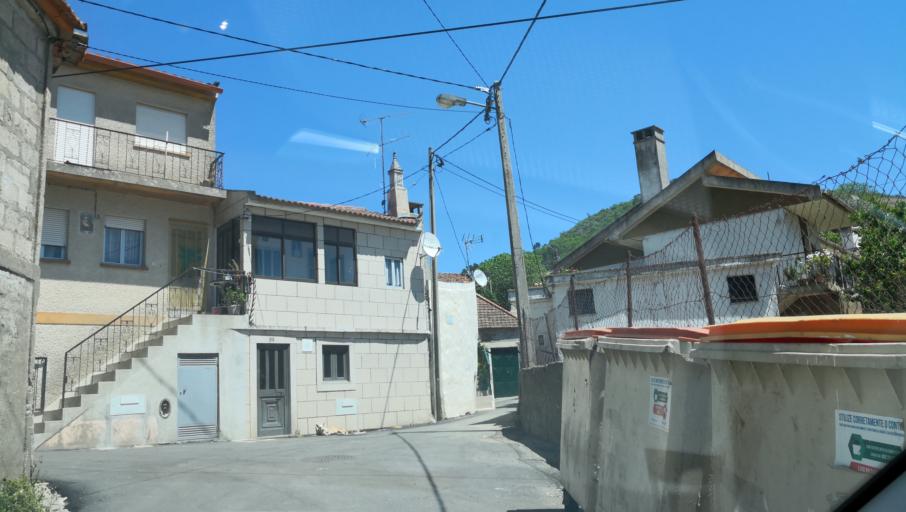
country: PT
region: Vila Real
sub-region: Vila Real
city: Vila Real
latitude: 41.2262
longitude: -7.7201
